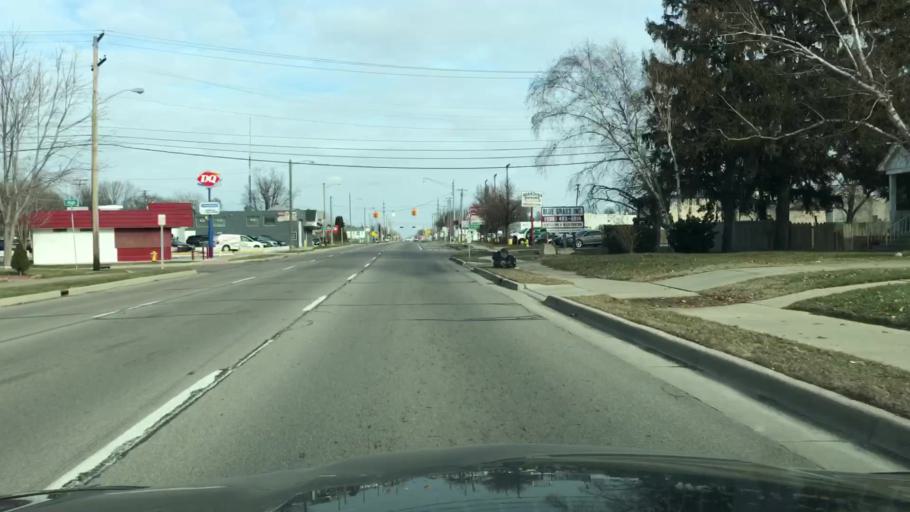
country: US
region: Michigan
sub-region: Macomb County
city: Mount Clemens
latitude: 42.6087
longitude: -82.8718
